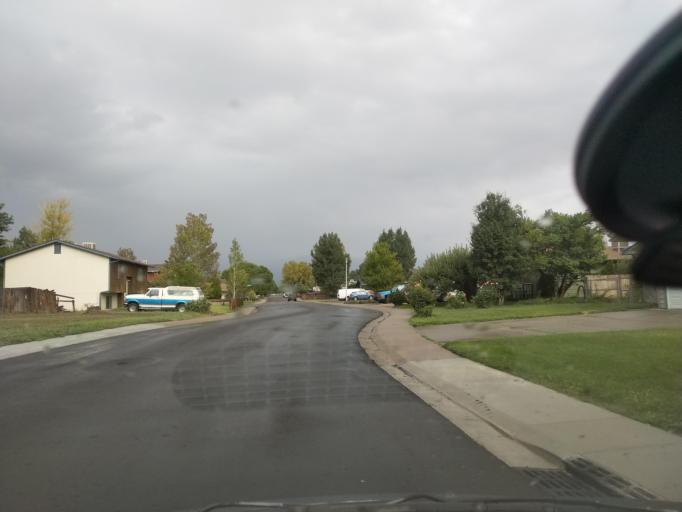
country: US
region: Colorado
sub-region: Mesa County
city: Fruitvale
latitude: 39.0741
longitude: -108.4862
